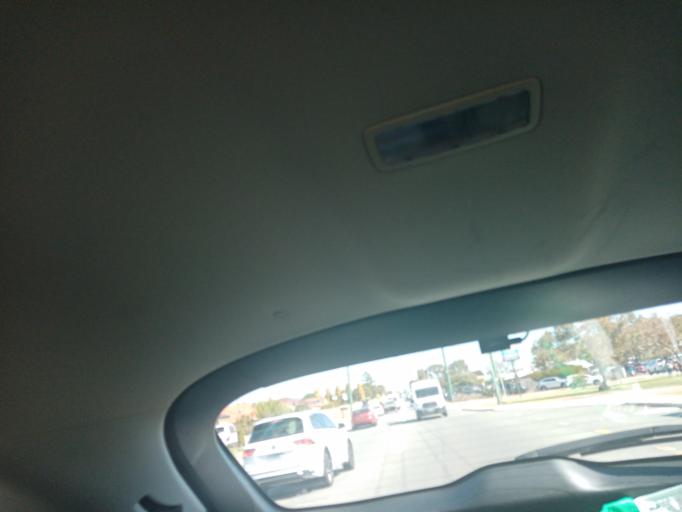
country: AU
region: Western Australia
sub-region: City of Cockburn
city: Spearwood
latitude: -32.1198
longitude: 115.7826
